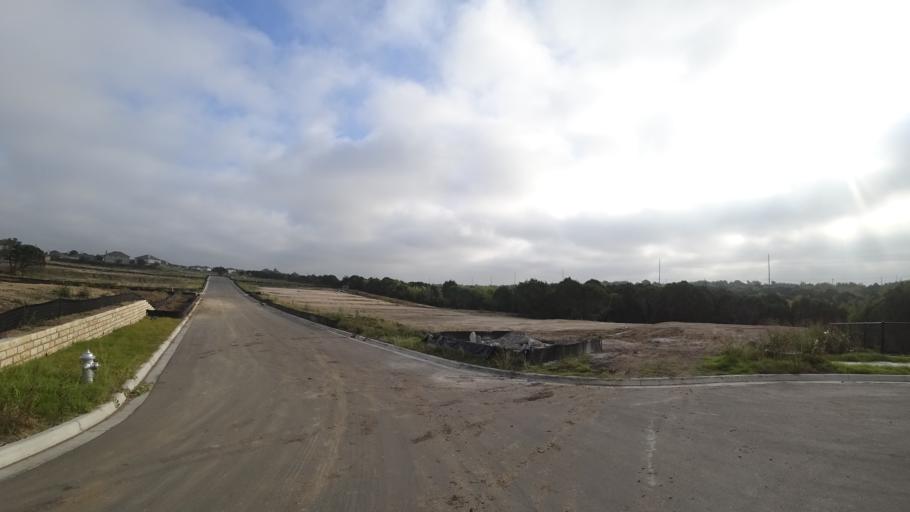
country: US
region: Texas
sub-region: Travis County
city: Manor
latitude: 30.3552
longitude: -97.6413
